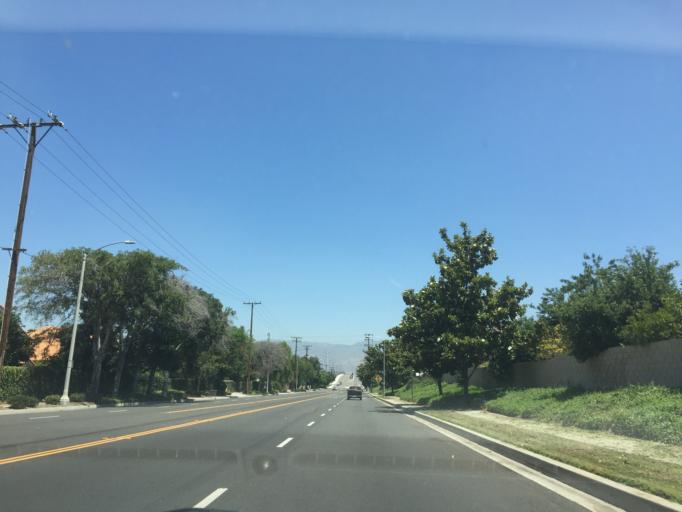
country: US
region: California
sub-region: San Bernardino County
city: Loma Linda
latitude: 34.0536
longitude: -117.2873
